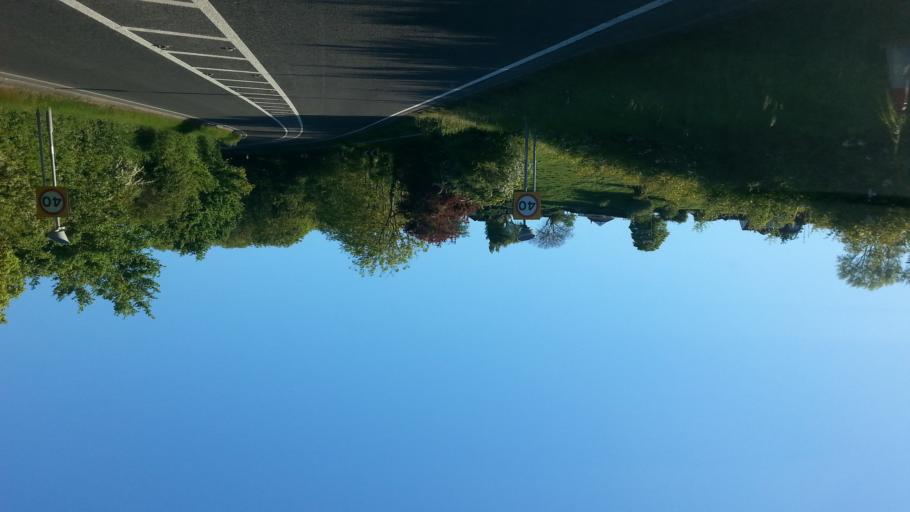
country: GB
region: England
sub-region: Bath and North East Somerset
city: Publow
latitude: 51.3898
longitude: -2.5510
